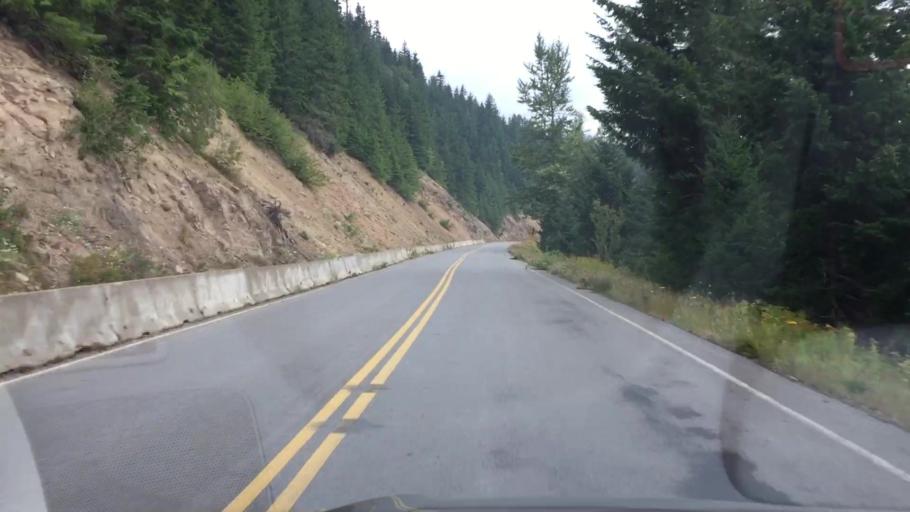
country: US
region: Washington
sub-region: Klickitat County
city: White Salmon
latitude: 46.1547
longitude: -121.6294
